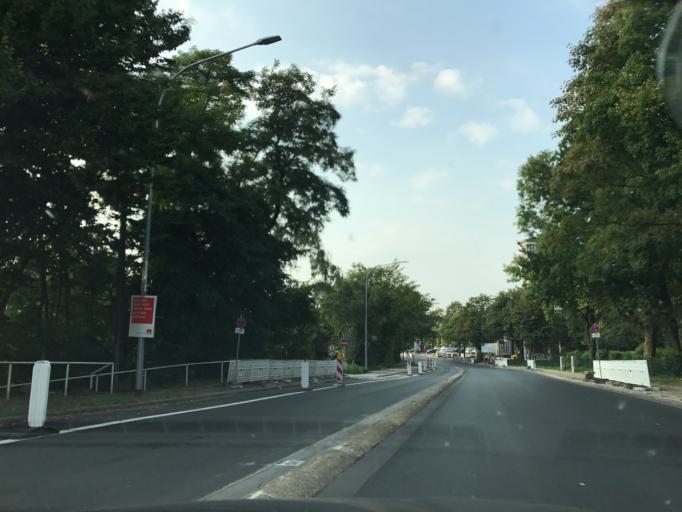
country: DE
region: North Rhine-Westphalia
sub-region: Regierungsbezirk Dusseldorf
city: Essen
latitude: 51.4398
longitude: 6.9790
